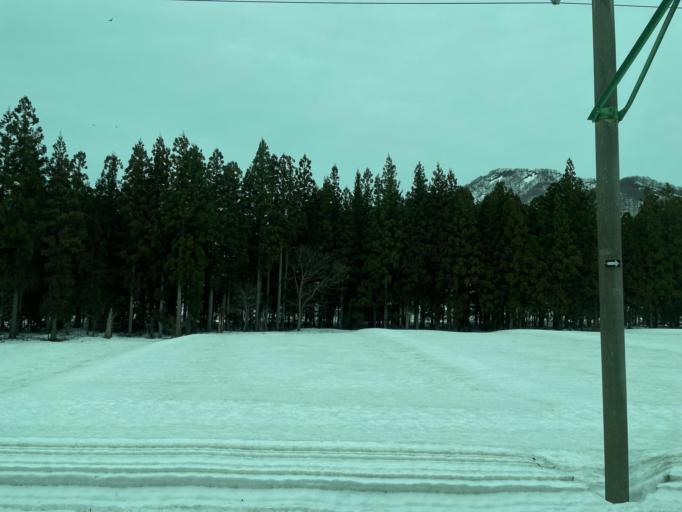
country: JP
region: Niigata
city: Shiozawa
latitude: 36.9300
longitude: 138.8492
